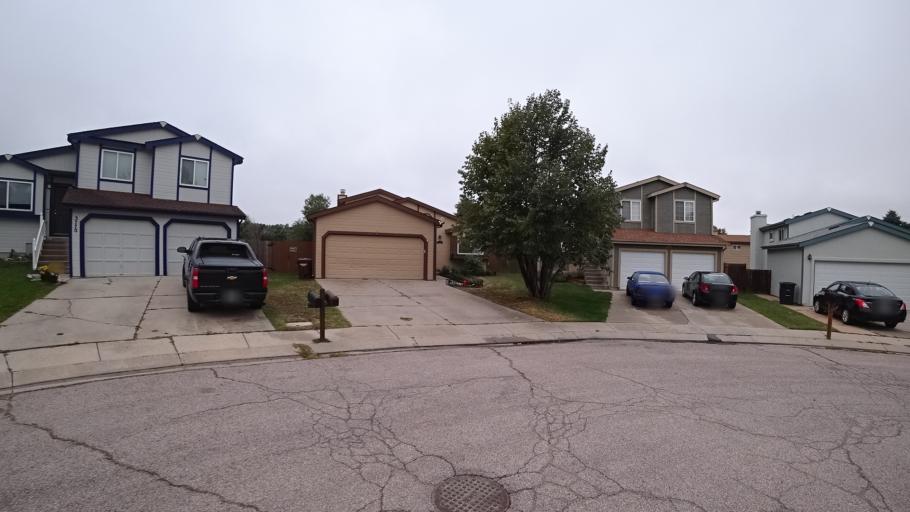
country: US
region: Colorado
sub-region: El Paso County
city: Cimarron Hills
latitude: 38.9315
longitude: -104.7601
